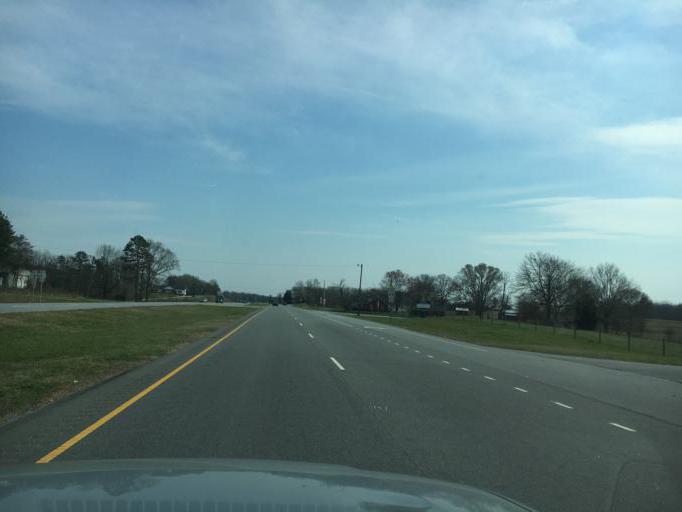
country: US
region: North Carolina
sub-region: Rutherford County
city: Forest City
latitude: 35.2763
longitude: -81.8954
